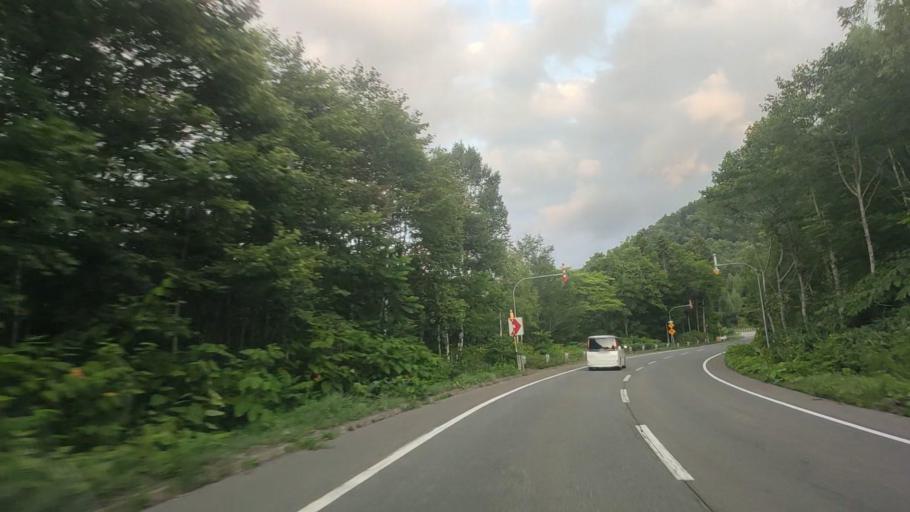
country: JP
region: Hokkaido
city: Ashibetsu
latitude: 43.3797
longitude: 142.1859
